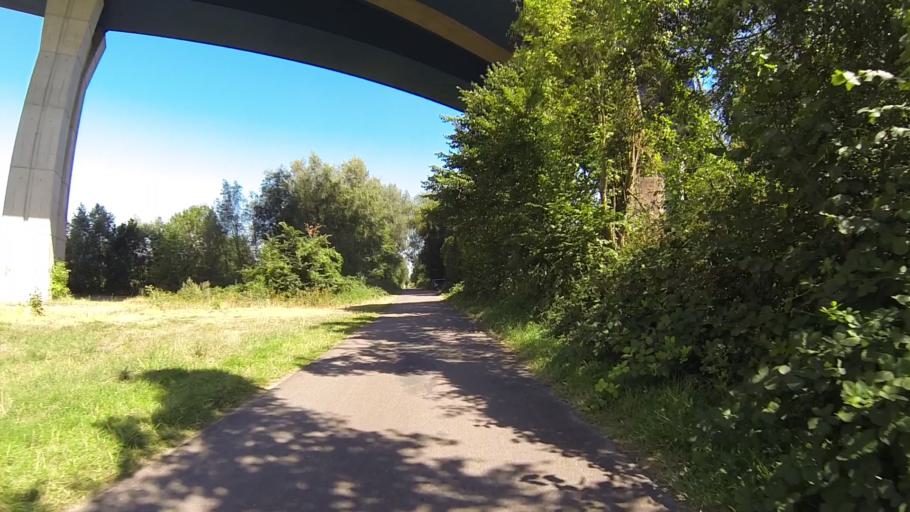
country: LU
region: Grevenmacher
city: Schengen
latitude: 49.4794
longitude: 6.3689
